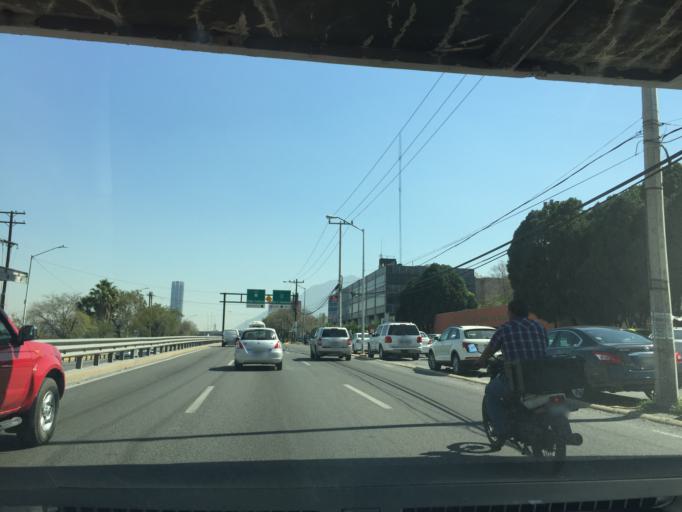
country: MX
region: Nuevo Leon
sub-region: Monterrey
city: Monterrey
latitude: 25.6665
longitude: -100.3382
